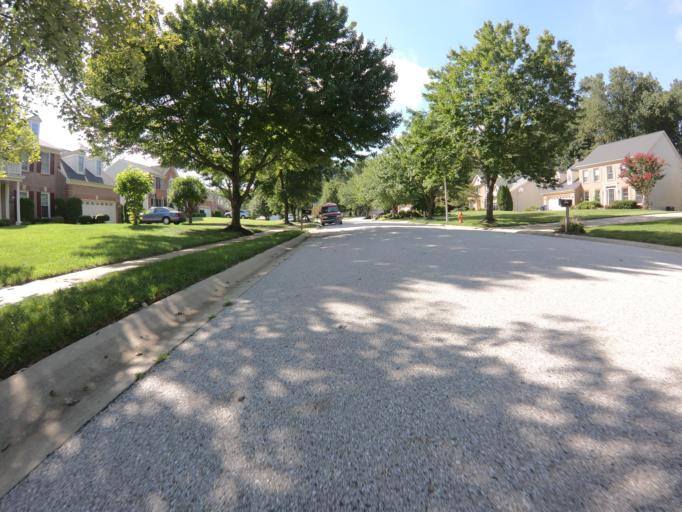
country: US
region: Maryland
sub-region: Howard County
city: Columbia
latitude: 39.2596
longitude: -76.8702
